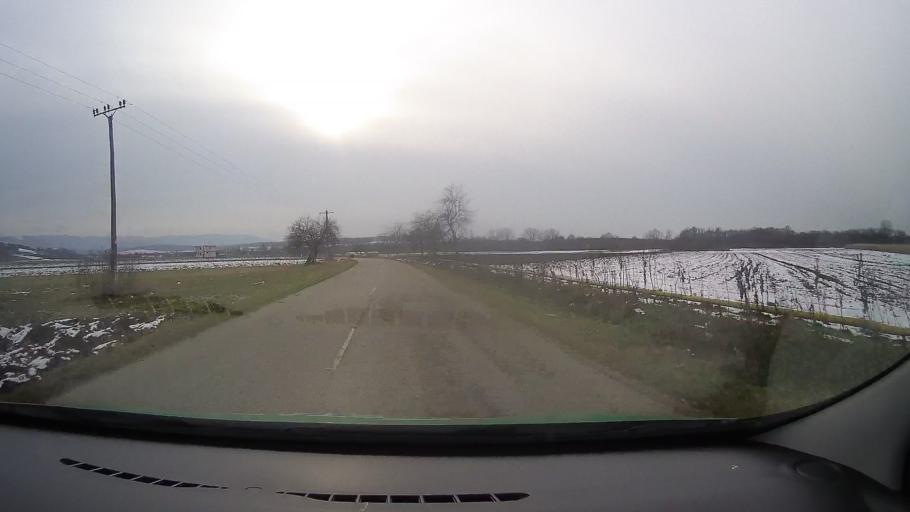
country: RO
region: Hunedoara
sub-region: Comuna Romos
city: Romos
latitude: 45.8616
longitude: 23.2731
